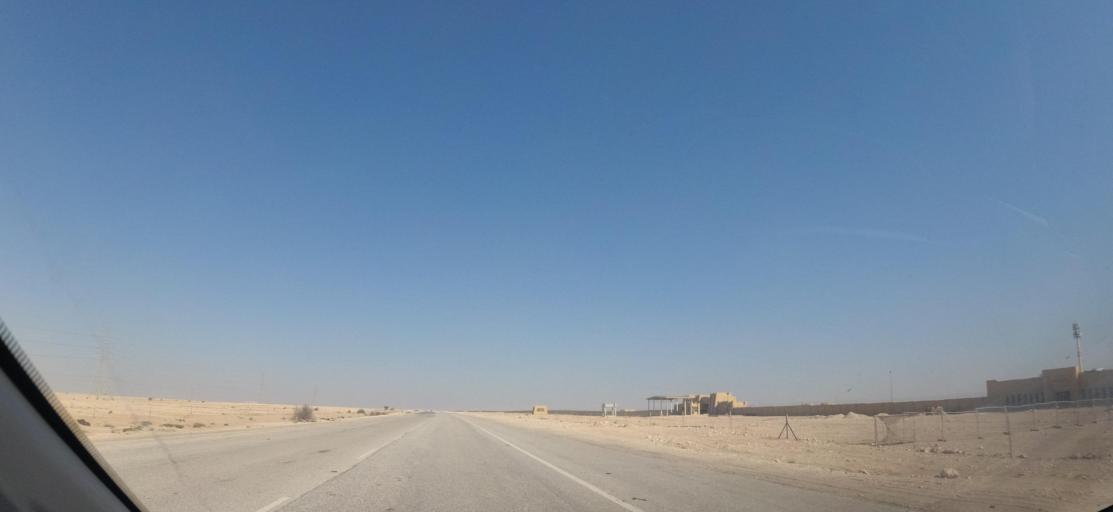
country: QA
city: Al Jumayliyah
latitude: 25.4847
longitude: 50.9722
